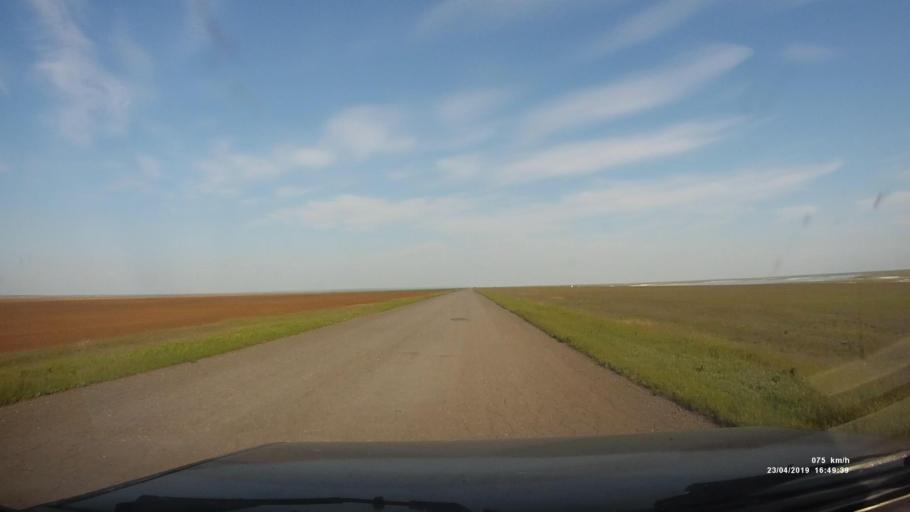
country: RU
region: Kalmykiya
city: Priyutnoye
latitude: 46.3302
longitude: 43.2798
